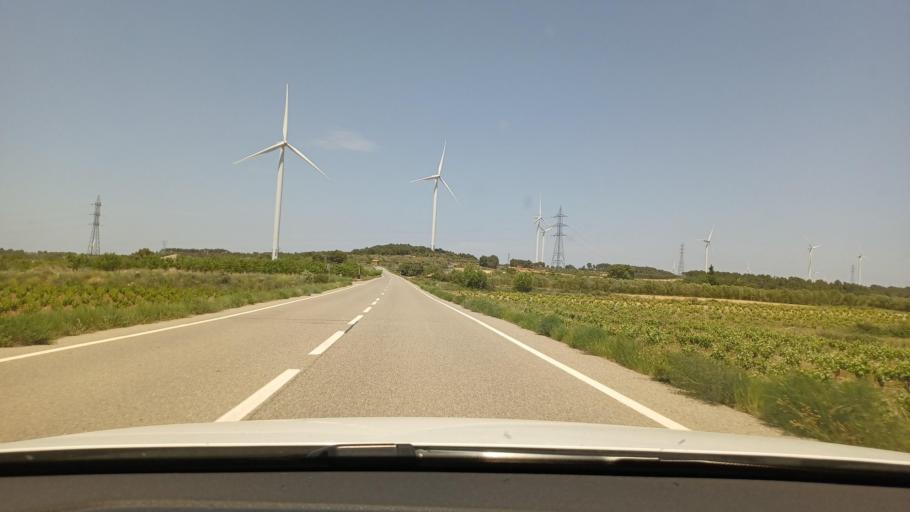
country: ES
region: Catalonia
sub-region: Provincia de Tarragona
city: Vilalba dels Arcs
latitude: 41.0961
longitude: 0.4182
